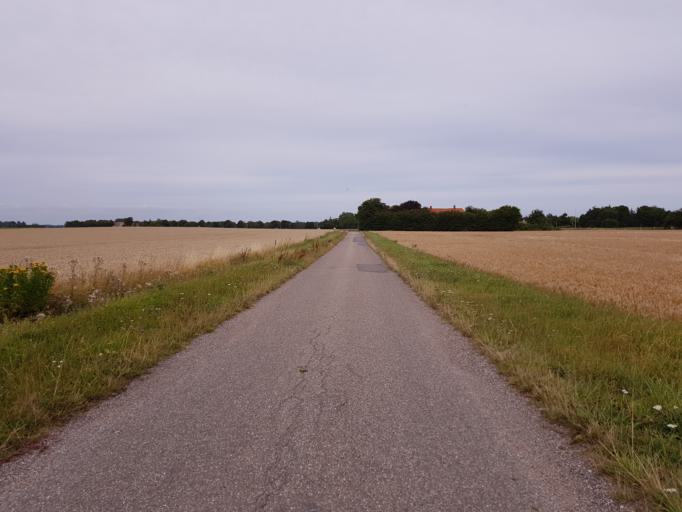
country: DK
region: Zealand
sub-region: Guldborgsund Kommune
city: Nykobing Falster
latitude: 54.5988
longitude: 11.9317
